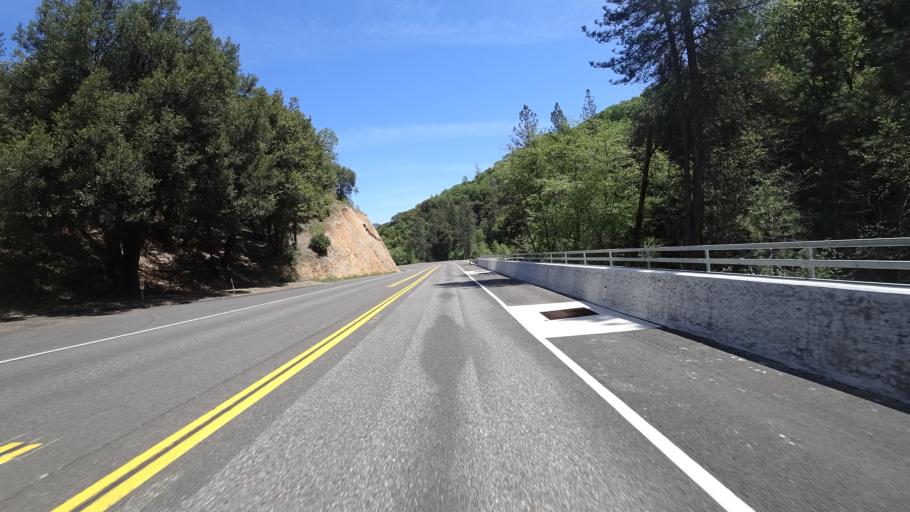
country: US
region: California
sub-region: Trinity County
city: Lewiston
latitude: 40.6732
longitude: -122.6750
